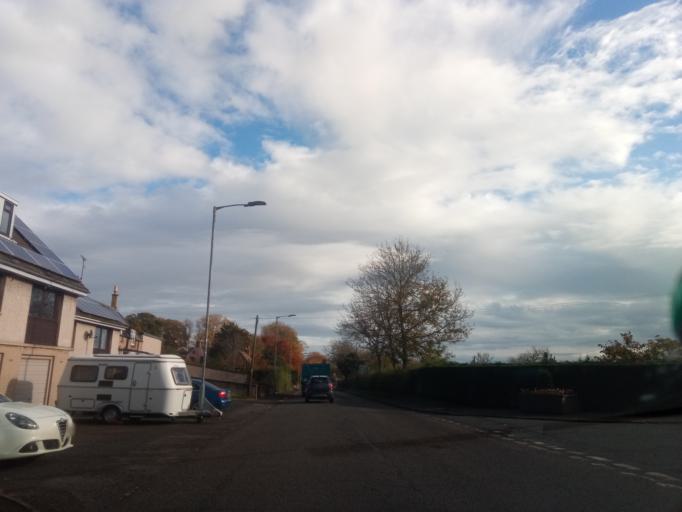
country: GB
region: Scotland
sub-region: The Scottish Borders
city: Coldstream
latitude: 55.7208
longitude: -2.2617
